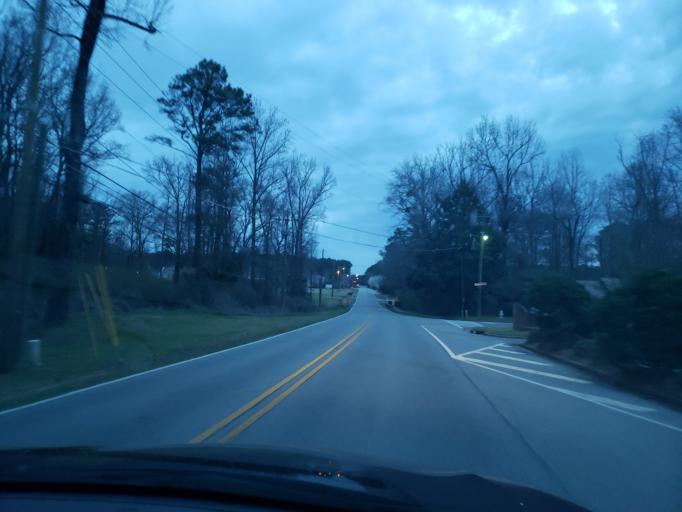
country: US
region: Alabama
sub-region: Lee County
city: Auburn
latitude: 32.6243
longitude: -85.4750
